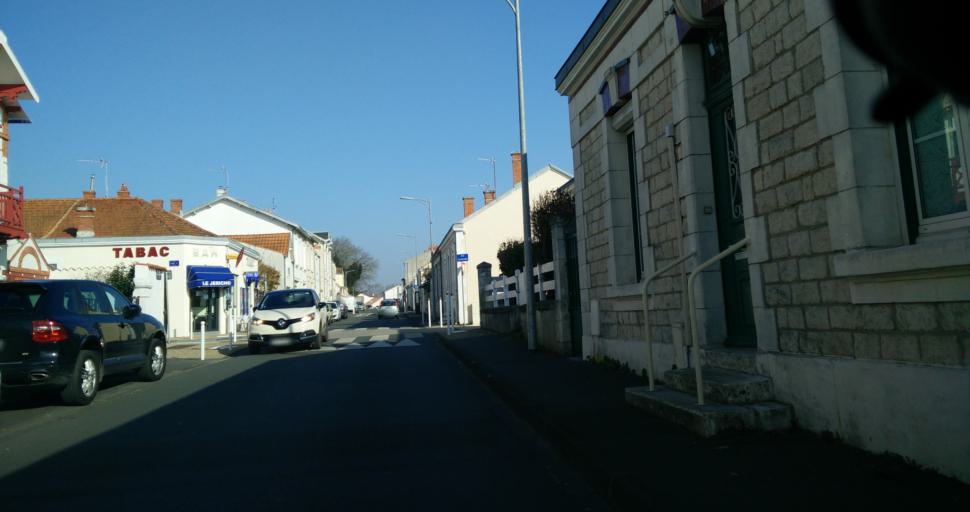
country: FR
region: Poitou-Charentes
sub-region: Departement de la Charente-Maritime
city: La Rochelle
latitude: 46.1672
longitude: -1.1594
